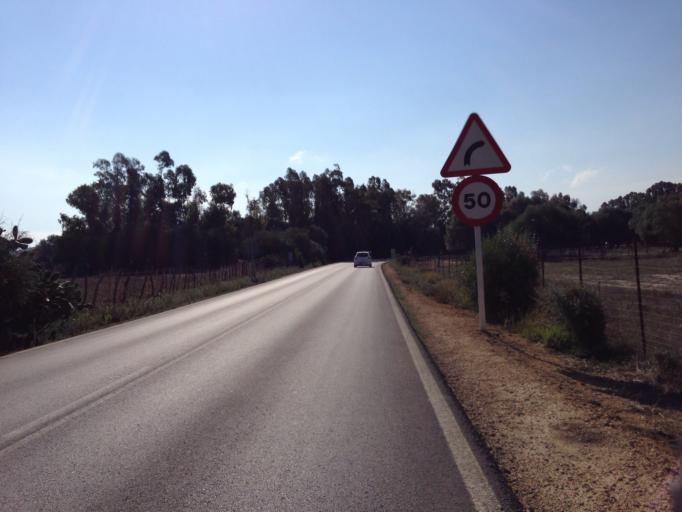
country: ES
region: Andalusia
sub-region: Provincia de Cadiz
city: Vejer de la Frontera
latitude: 36.2125
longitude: -6.0338
